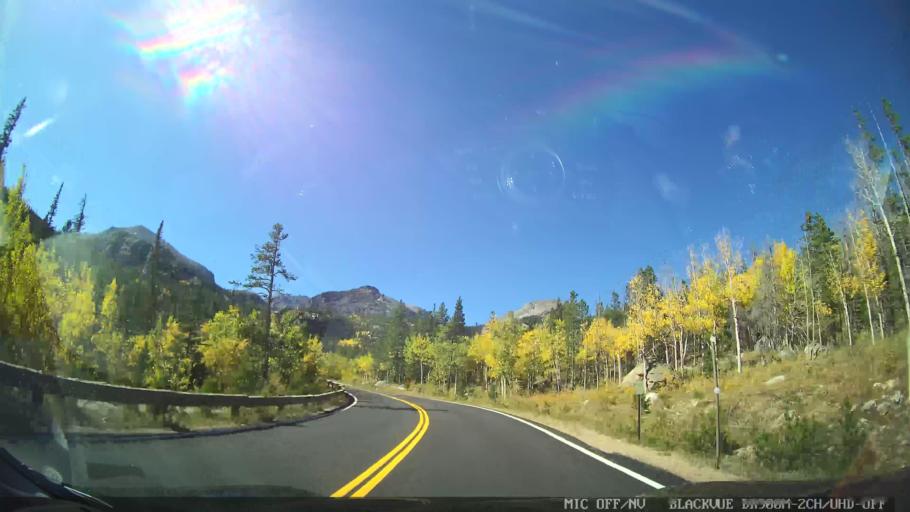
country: US
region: Colorado
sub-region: Larimer County
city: Estes Park
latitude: 40.3102
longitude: -105.6377
